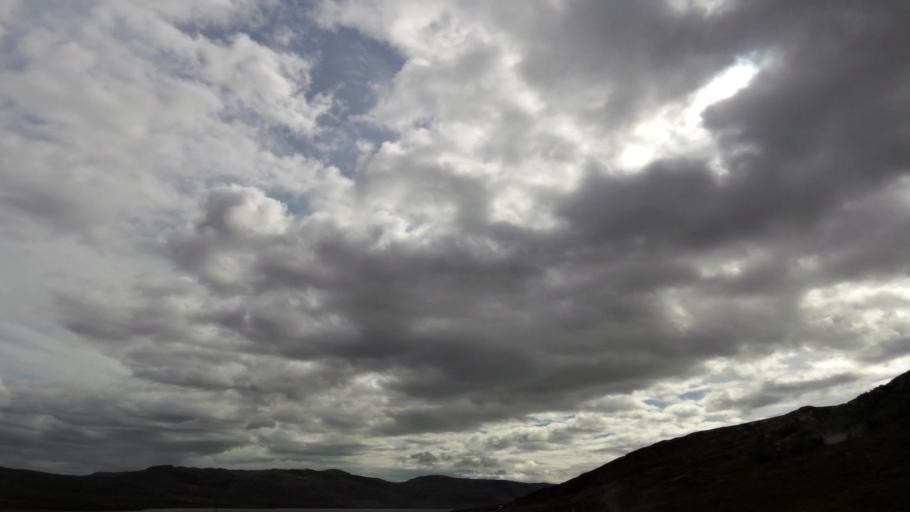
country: IS
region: West
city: Stykkisholmur
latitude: 65.5840
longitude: -22.1578
